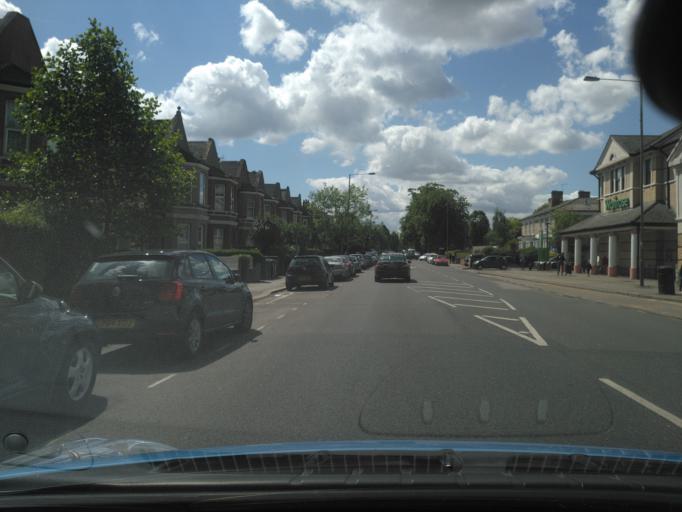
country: GB
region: England
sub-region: Greater London
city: Hendon
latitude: 51.6113
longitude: -0.1791
